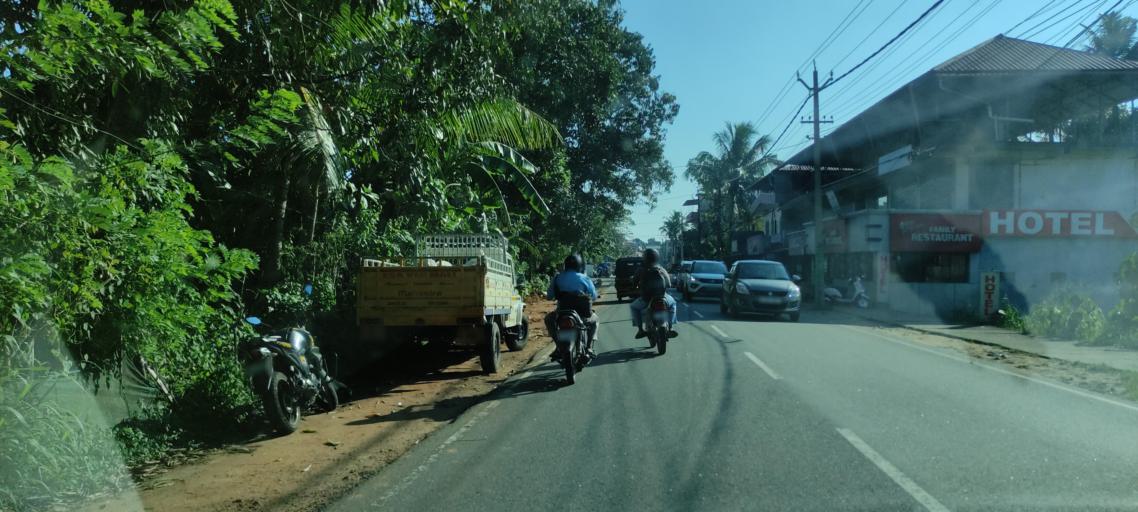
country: IN
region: Kerala
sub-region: Pattanamtitta
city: Pathanamthitta
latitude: 9.2443
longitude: 76.7565
